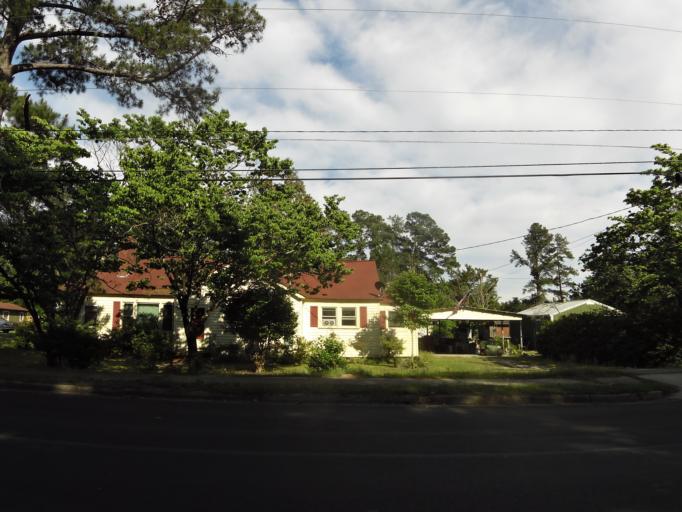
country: US
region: South Carolina
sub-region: Allendale County
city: Fairfax
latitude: 32.9696
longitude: -81.2334
